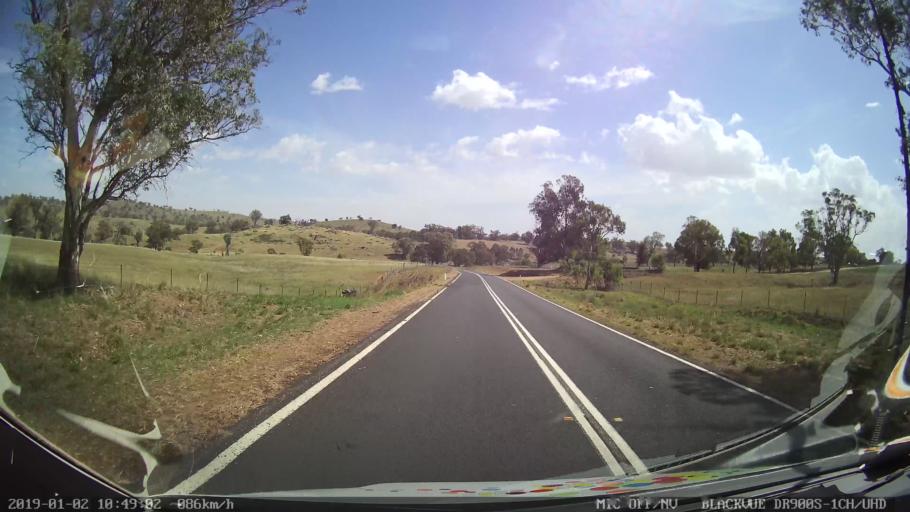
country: AU
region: New South Wales
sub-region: Cootamundra
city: Cootamundra
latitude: -34.7297
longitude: 148.2777
